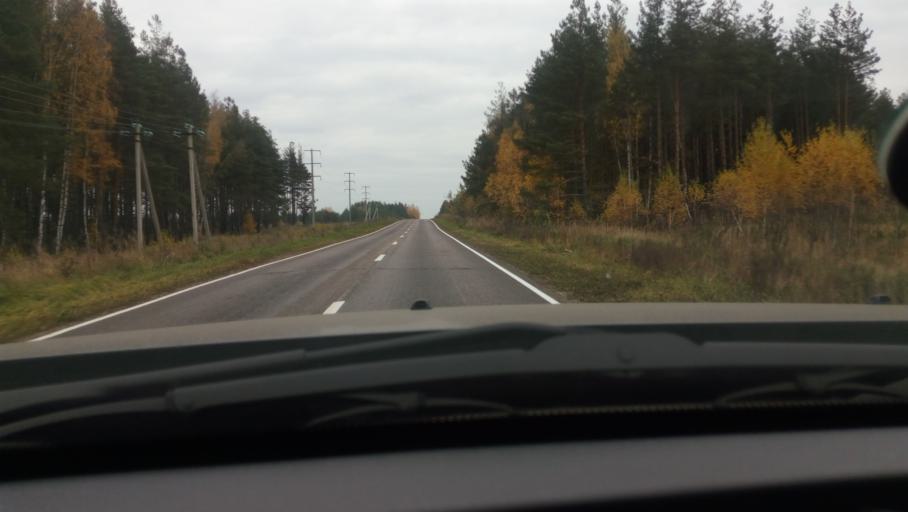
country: RU
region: Moskovskaya
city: Avsyunino
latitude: 55.5984
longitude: 39.2268
